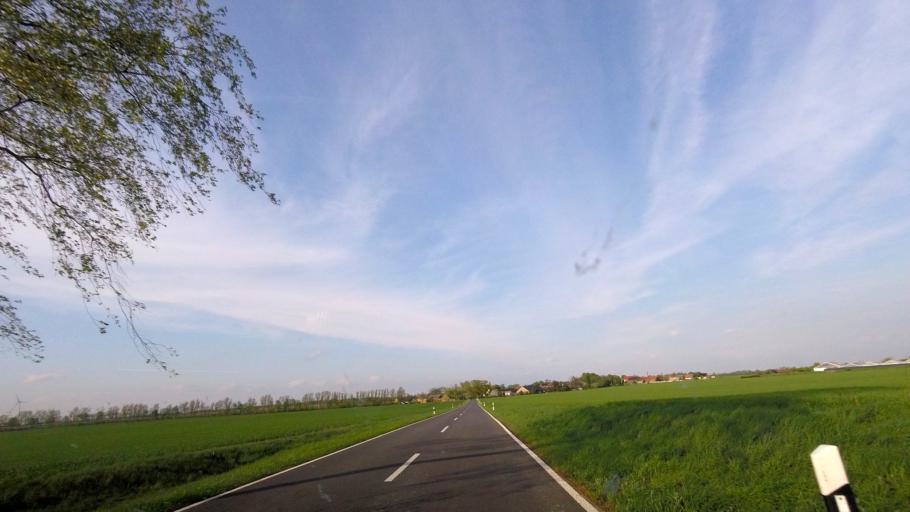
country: DE
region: Saxony-Anhalt
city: Zahna
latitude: 51.9648
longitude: 12.8548
